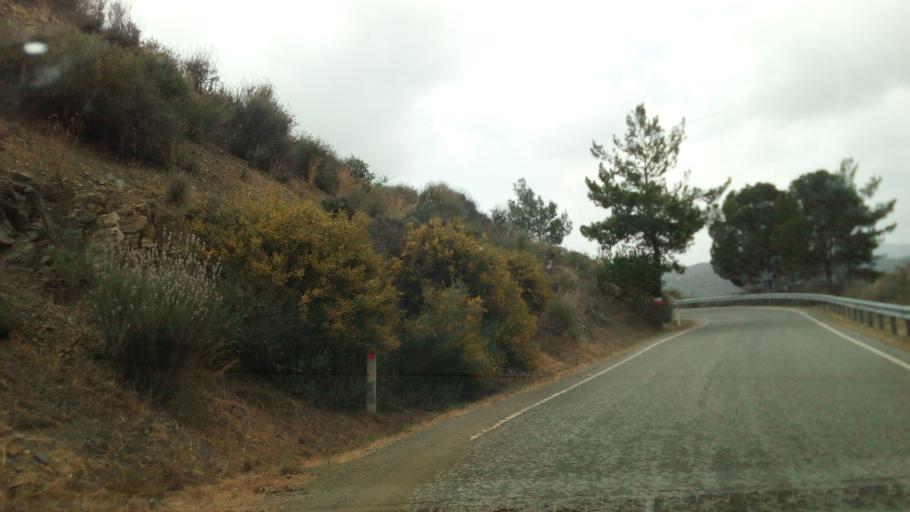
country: CY
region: Limassol
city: Parekklisha
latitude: 34.8653
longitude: 33.1854
